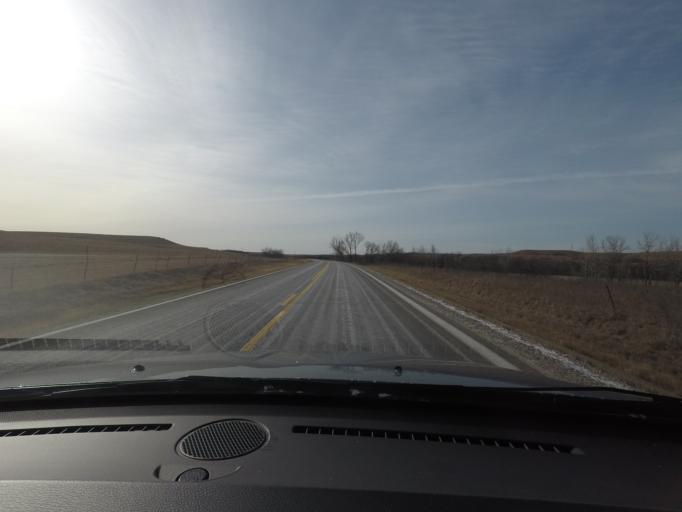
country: US
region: Kansas
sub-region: Riley County
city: Manhattan
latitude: 39.0133
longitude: -96.5361
